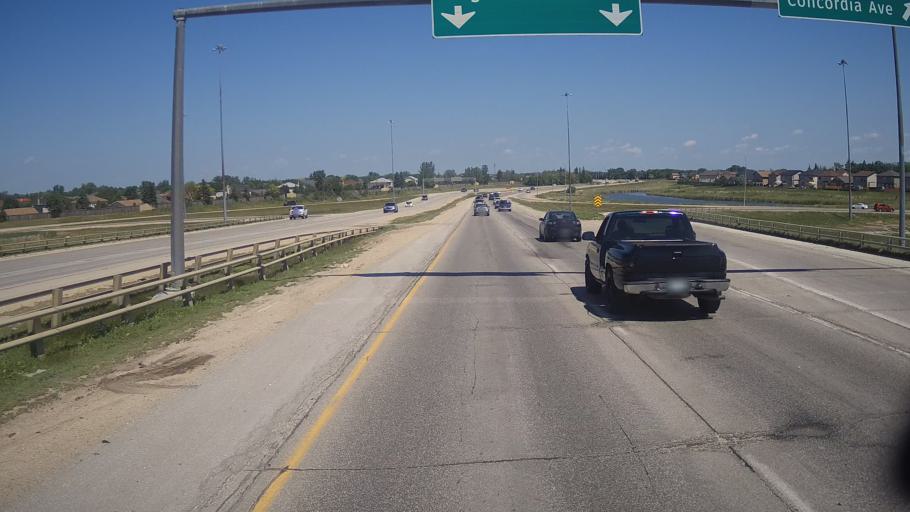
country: CA
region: Manitoba
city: Winnipeg
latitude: 49.9118
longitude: -97.0558
